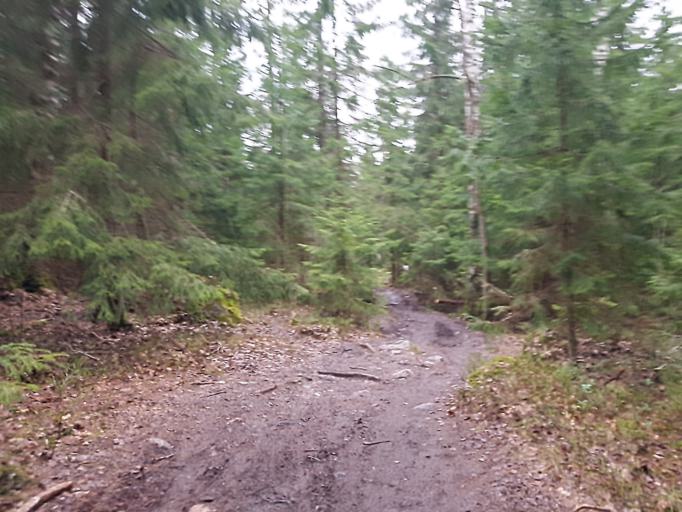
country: FI
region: Uusimaa
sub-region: Helsinki
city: Helsinki
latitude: 60.2621
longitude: 24.9211
